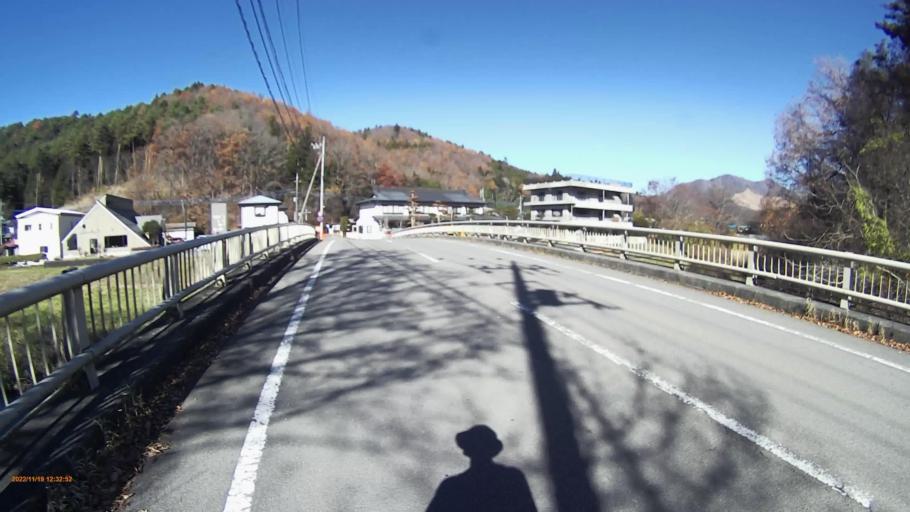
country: JP
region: Yamanashi
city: Fujikawaguchiko
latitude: 35.4563
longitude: 138.8246
